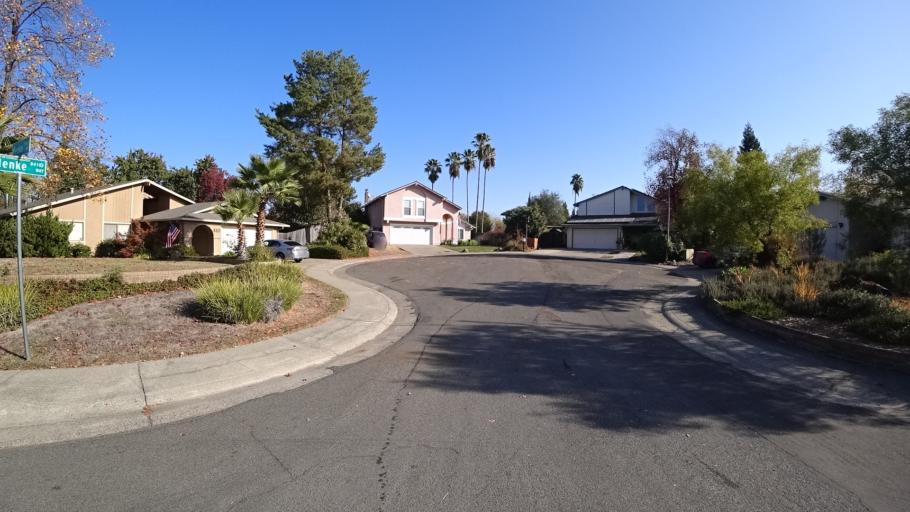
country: US
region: California
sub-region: Sacramento County
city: Orangevale
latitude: 38.6991
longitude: -121.2483
